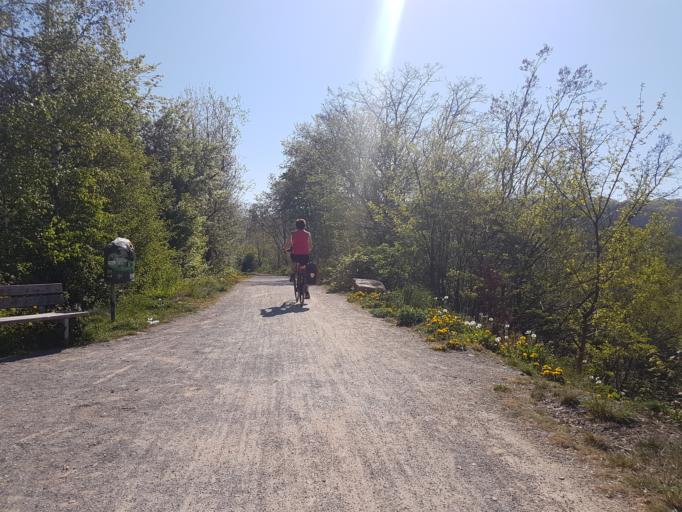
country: DE
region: North Rhine-Westphalia
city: Hattingen
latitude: 51.3893
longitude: 7.1760
